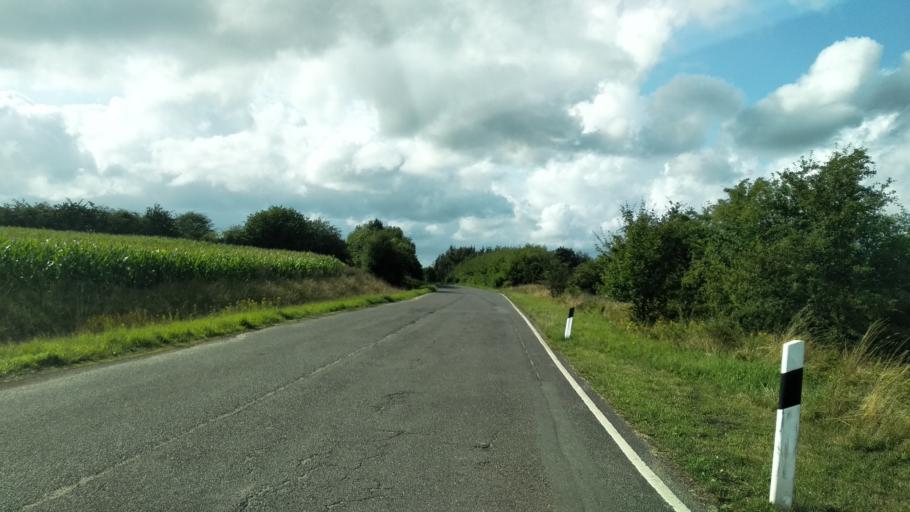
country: DE
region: Schleswig-Holstein
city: Neuberend
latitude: 54.5479
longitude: 9.5436
